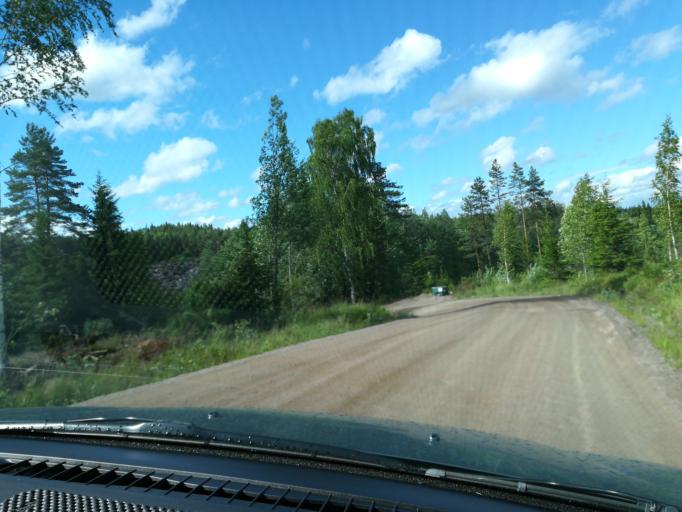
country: FI
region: South Karelia
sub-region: Lappeenranta
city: Savitaipale
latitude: 61.3007
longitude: 27.6397
